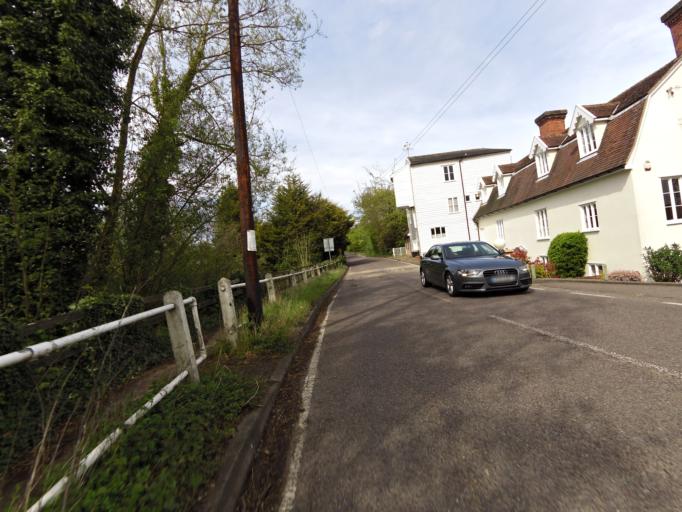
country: GB
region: England
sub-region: Suffolk
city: Ipswich
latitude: 51.9778
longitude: 1.1576
